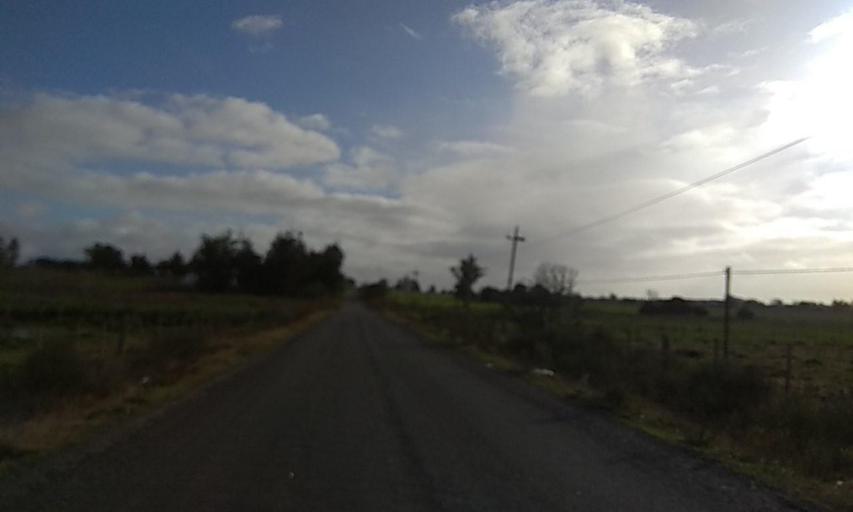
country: UY
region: Florida
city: Florida
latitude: -34.0504
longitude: -56.1895
